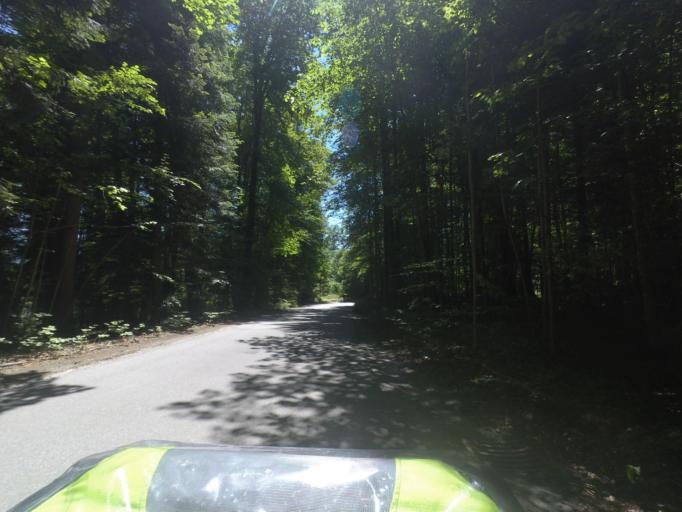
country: AT
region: Salzburg
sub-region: Politischer Bezirk Hallein
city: Oberalm
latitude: 47.7048
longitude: 13.1165
